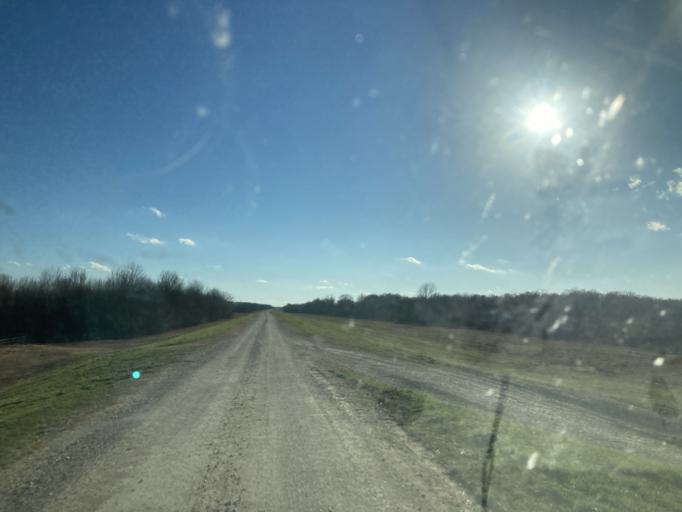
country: US
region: Mississippi
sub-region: Yazoo County
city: Yazoo City
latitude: 32.9362
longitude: -90.5465
